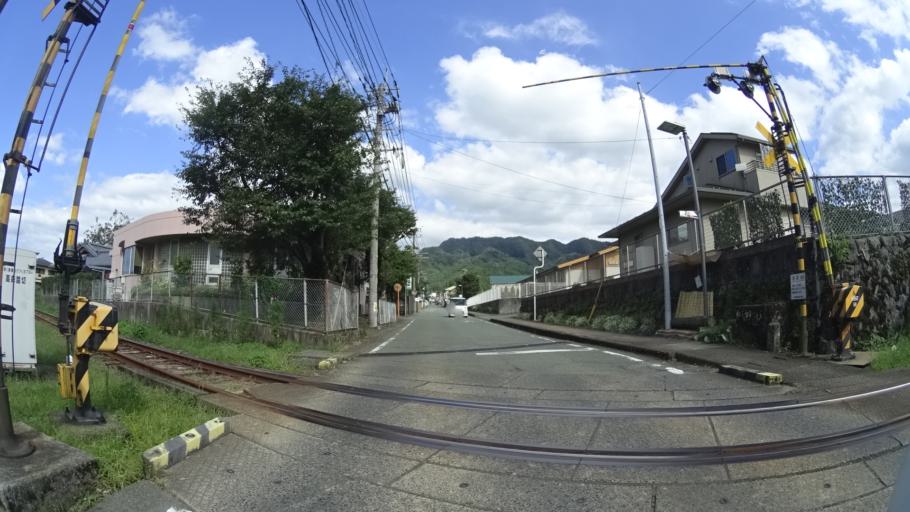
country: JP
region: Kumamoto
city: Aso
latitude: 32.8165
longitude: 131.1221
